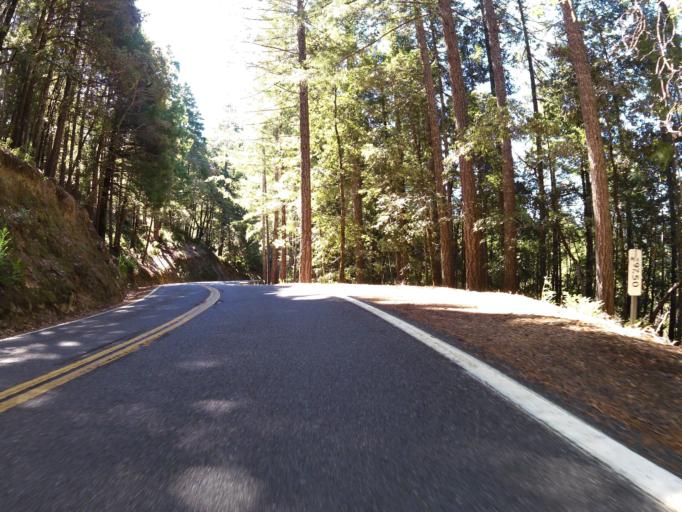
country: US
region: California
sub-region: Humboldt County
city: Redway
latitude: 39.8259
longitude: -123.7792
